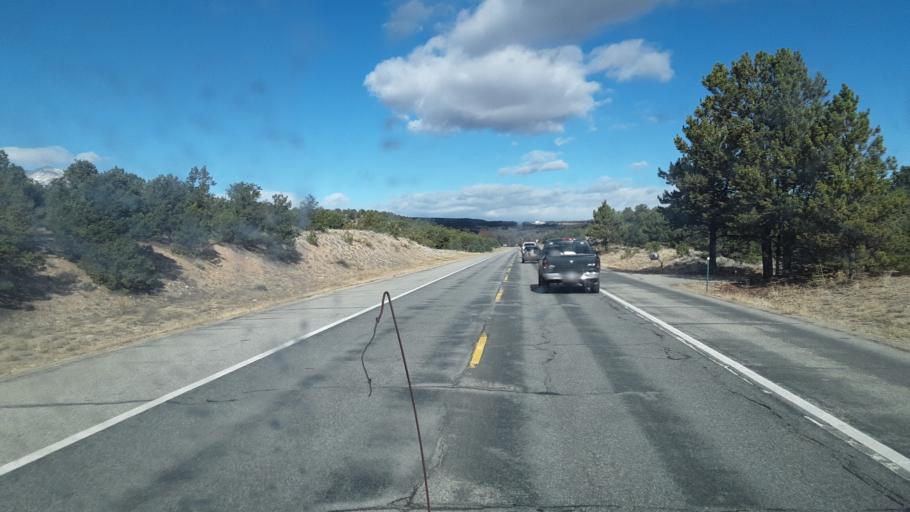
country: US
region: Colorado
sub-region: Chaffee County
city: Salida
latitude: 38.6280
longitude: -106.0780
